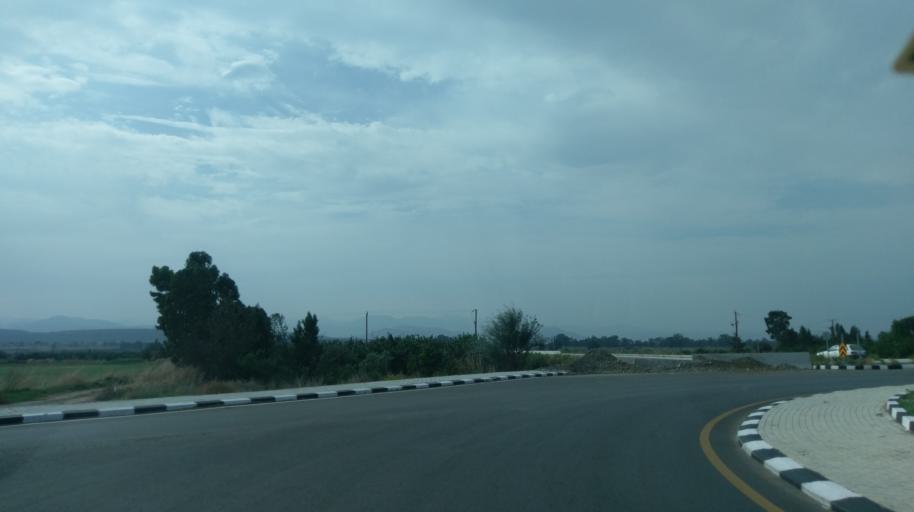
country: CY
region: Lefkosia
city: Lefka
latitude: 35.1539
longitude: 32.9062
